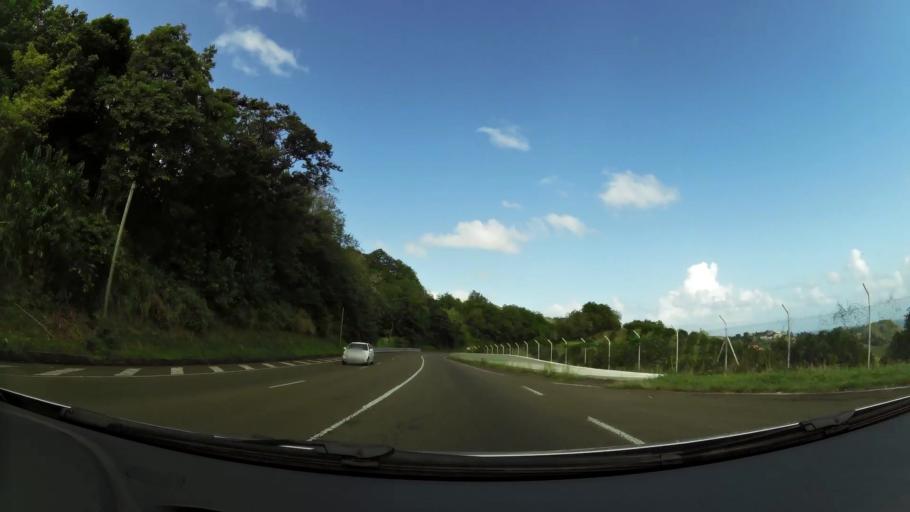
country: MQ
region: Martinique
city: Petite Riviere Salee
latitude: 14.7557
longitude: -60.9787
